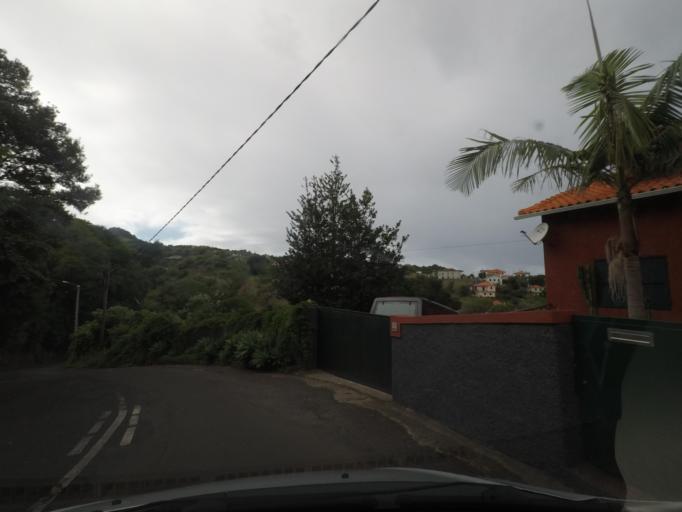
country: PT
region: Madeira
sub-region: Santana
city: Santana
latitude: 32.8298
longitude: -16.9065
